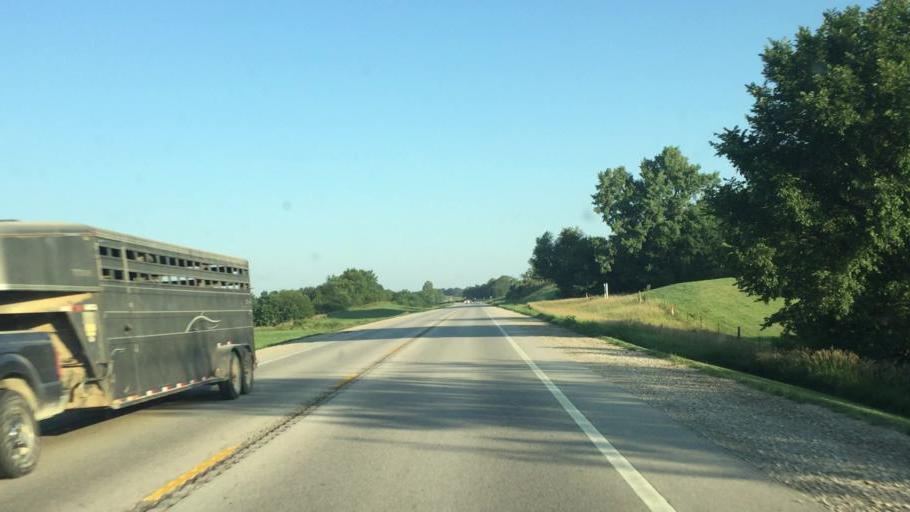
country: US
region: Kansas
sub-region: Doniphan County
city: Troy
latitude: 39.7900
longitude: -95.0441
